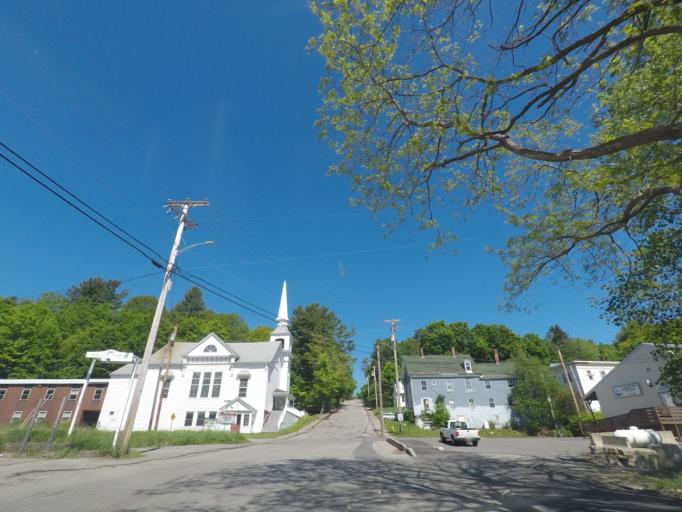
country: US
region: Maine
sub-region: Kennebec County
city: Gardiner
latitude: 44.2299
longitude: -69.7775
